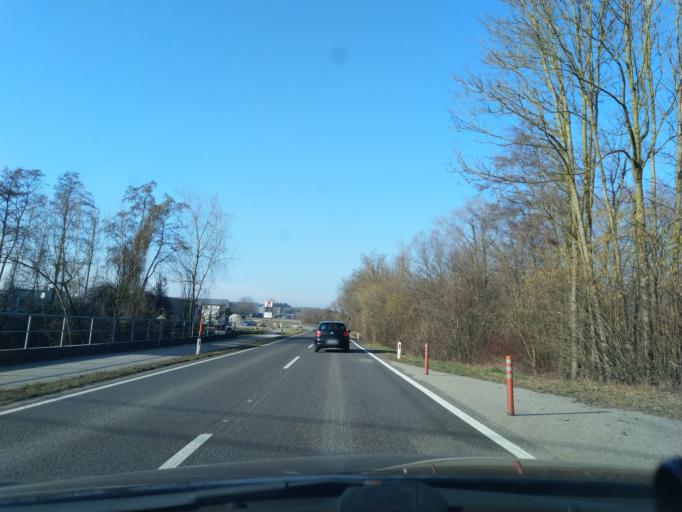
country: AT
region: Upper Austria
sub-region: Politischer Bezirk Scharding
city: Sankt Marienkirchen bei Schaerding
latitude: 48.3073
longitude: 13.4268
